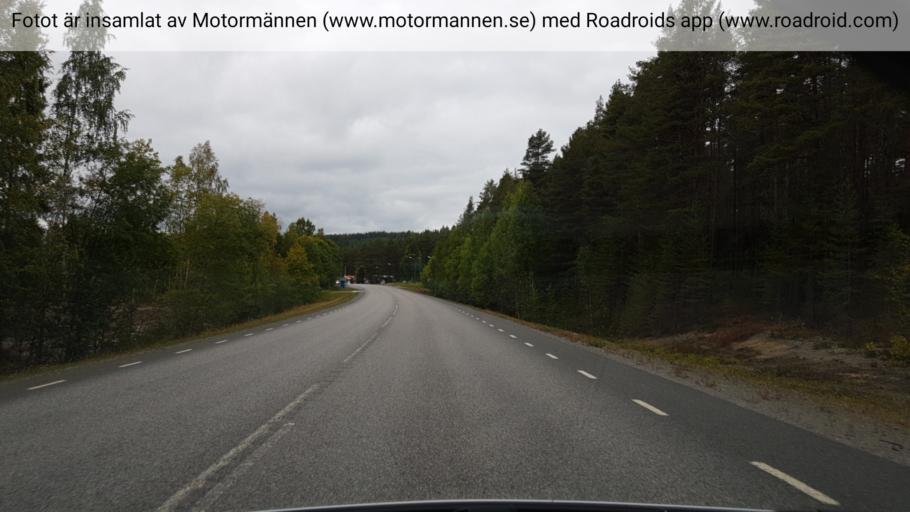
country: SE
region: Vaesterbotten
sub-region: Skelleftea Kommun
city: Langsele
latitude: 64.9149
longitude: 20.1032
